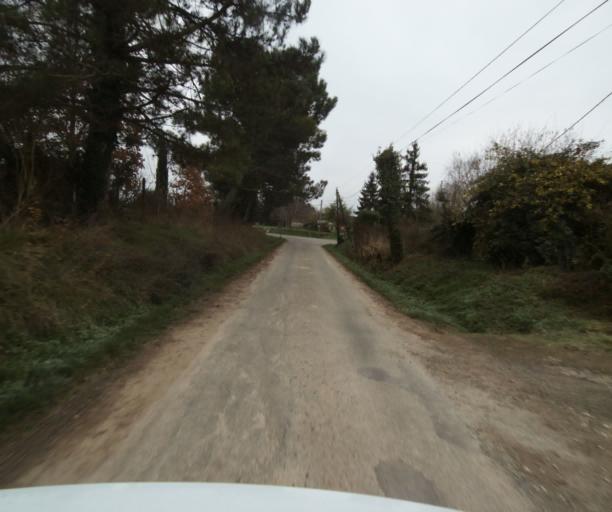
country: FR
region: Midi-Pyrenees
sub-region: Departement du Tarn-et-Garonne
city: Moissac
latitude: 44.1122
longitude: 1.1453
